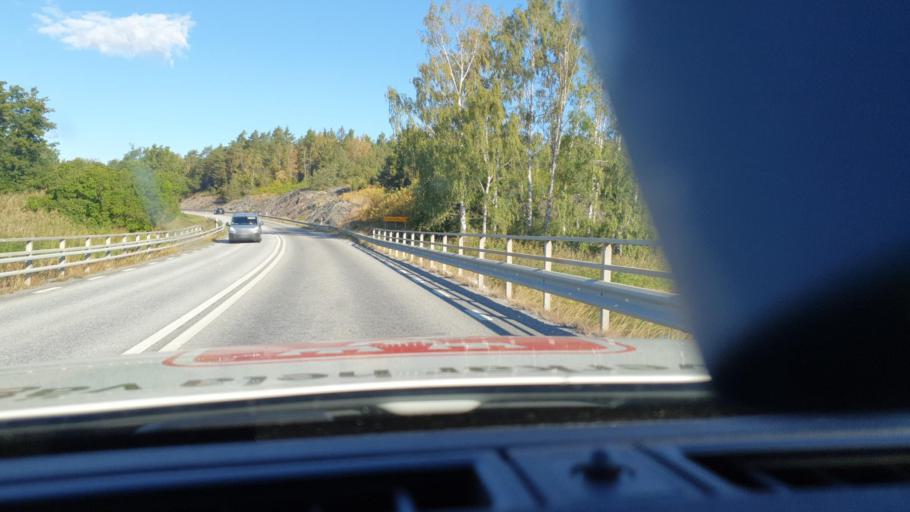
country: SE
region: Stockholm
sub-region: Vaxholms Kommun
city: Resaro
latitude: 59.4209
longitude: 18.3001
